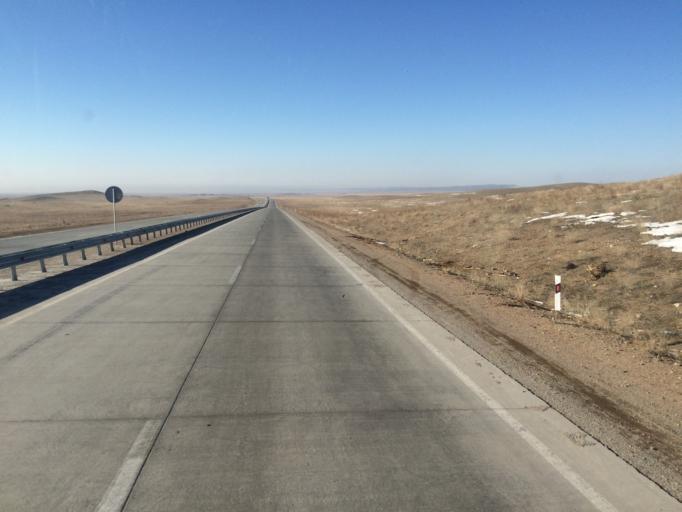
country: KZ
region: Zhambyl
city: Georgiyevka
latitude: 43.3396
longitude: 74.4605
